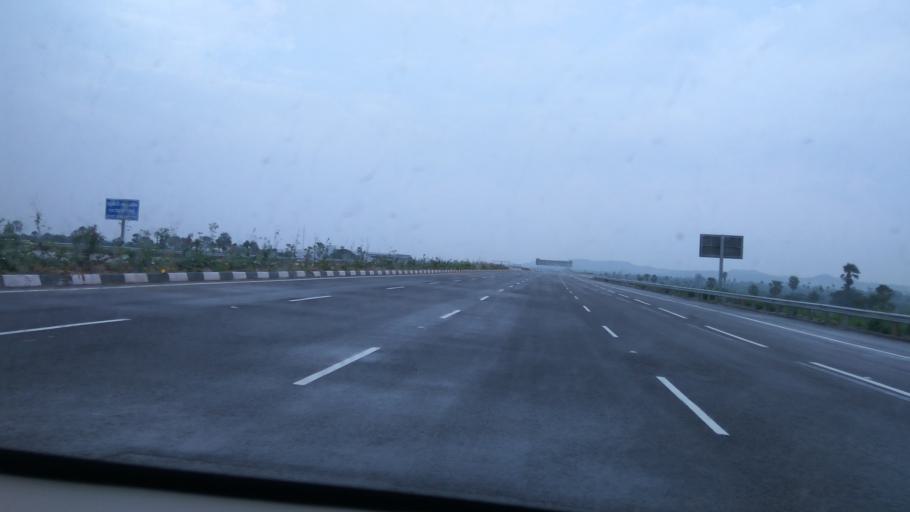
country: IN
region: Telangana
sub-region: Rangareddi
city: Ghatkesar
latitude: 17.4499
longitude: 78.6681
